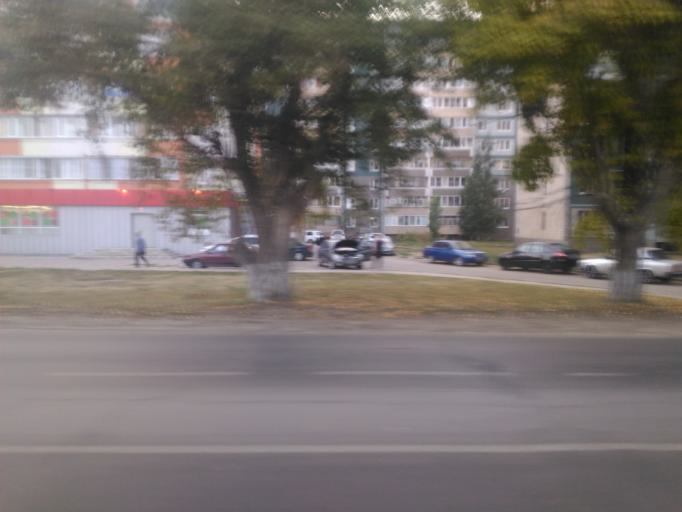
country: RU
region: Ulyanovsk
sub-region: Ulyanovskiy Rayon
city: Ulyanovsk
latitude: 54.2659
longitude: 48.2822
